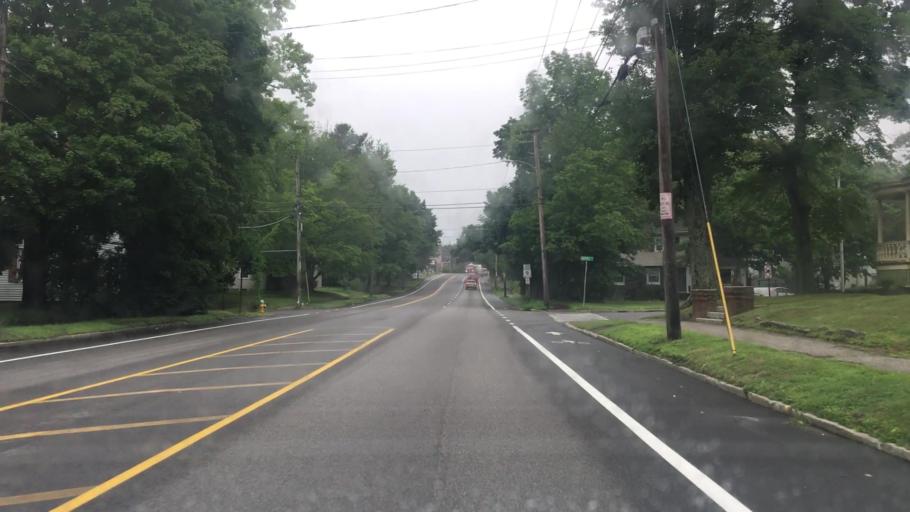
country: US
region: Maine
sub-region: Cumberland County
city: Portland
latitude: 43.6847
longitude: -70.2661
